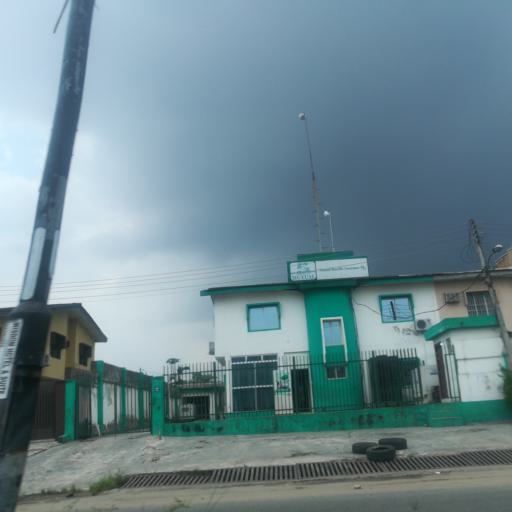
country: NG
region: Lagos
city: Ojota
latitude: 6.5799
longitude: 3.3865
